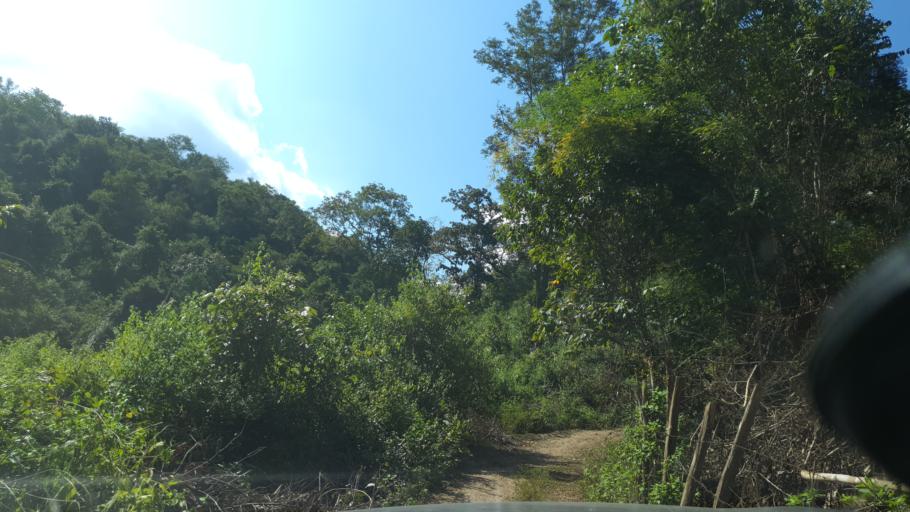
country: TH
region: Mae Hong Son
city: Mae Hi
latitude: 19.2984
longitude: 98.7033
